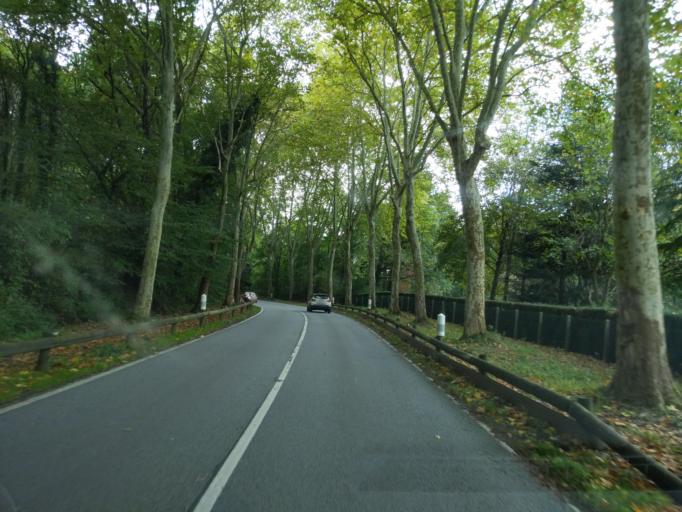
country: FR
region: Ile-de-France
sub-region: Departement des Yvelines
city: Chevreuse
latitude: 48.7016
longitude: 2.0313
